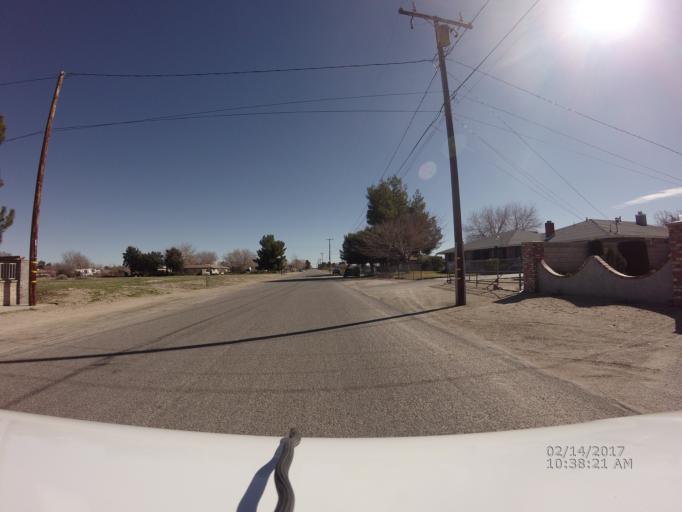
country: US
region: California
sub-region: Los Angeles County
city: Littlerock
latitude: 34.5634
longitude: -117.9414
